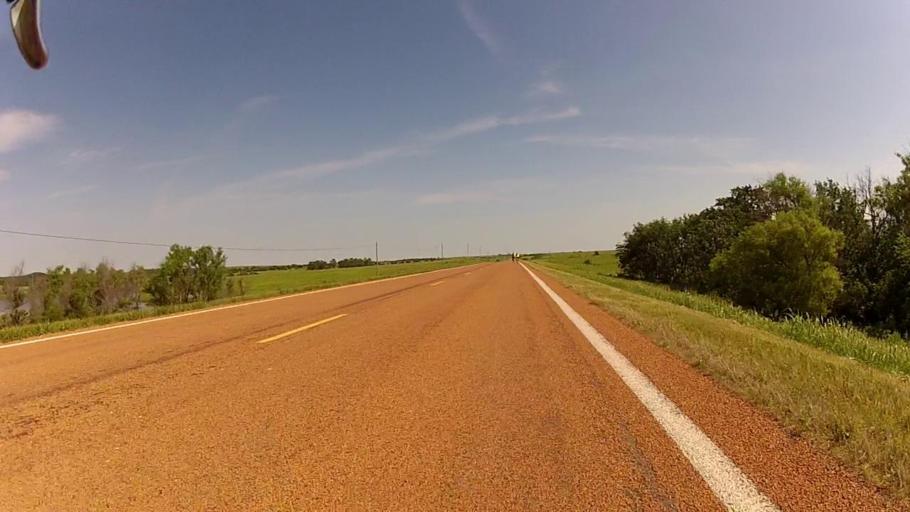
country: US
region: Kansas
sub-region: Cowley County
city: Winfield
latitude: 37.0843
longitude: -96.6436
